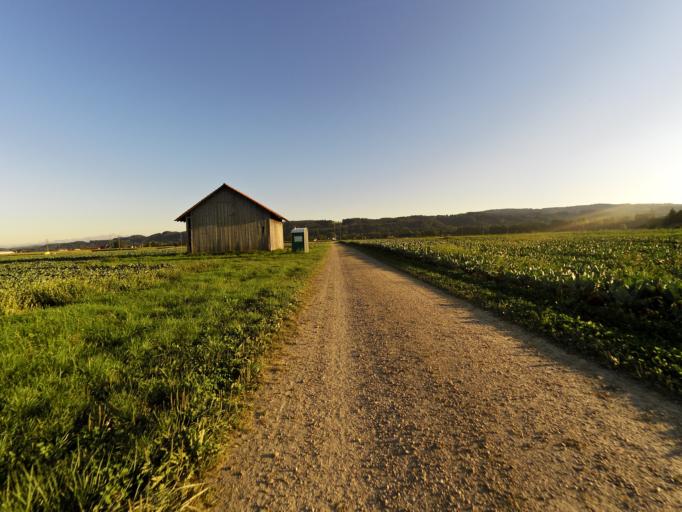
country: CH
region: Thurgau
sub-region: Weinfelden District
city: Wigoltingen
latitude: 47.5935
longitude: 9.0260
